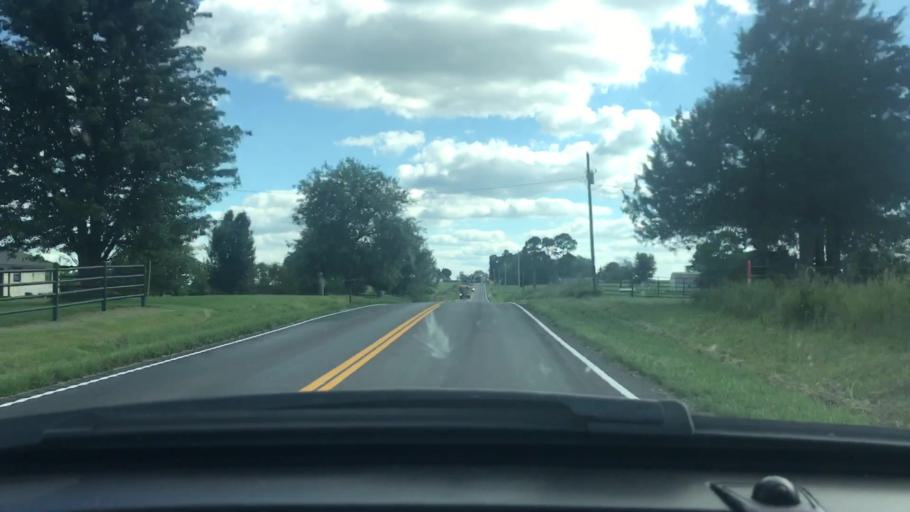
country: US
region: Missouri
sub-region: Wright County
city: Mountain Grove
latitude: 37.1716
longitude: -92.2671
